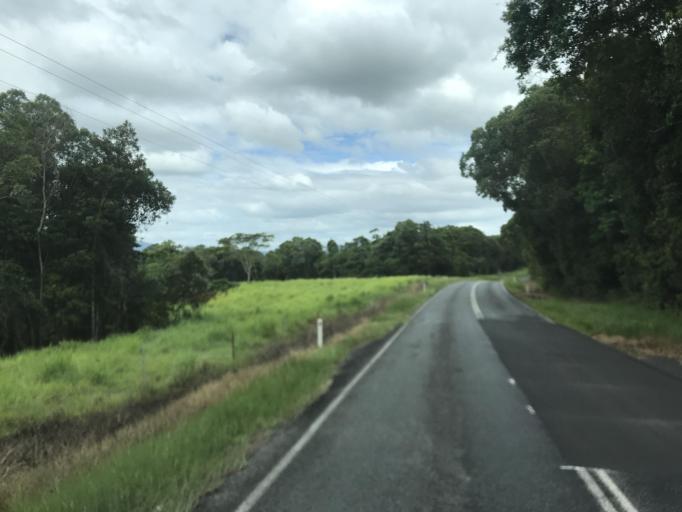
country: AU
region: Queensland
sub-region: Cassowary Coast
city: Innisfail
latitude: -17.8488
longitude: 146.0589
